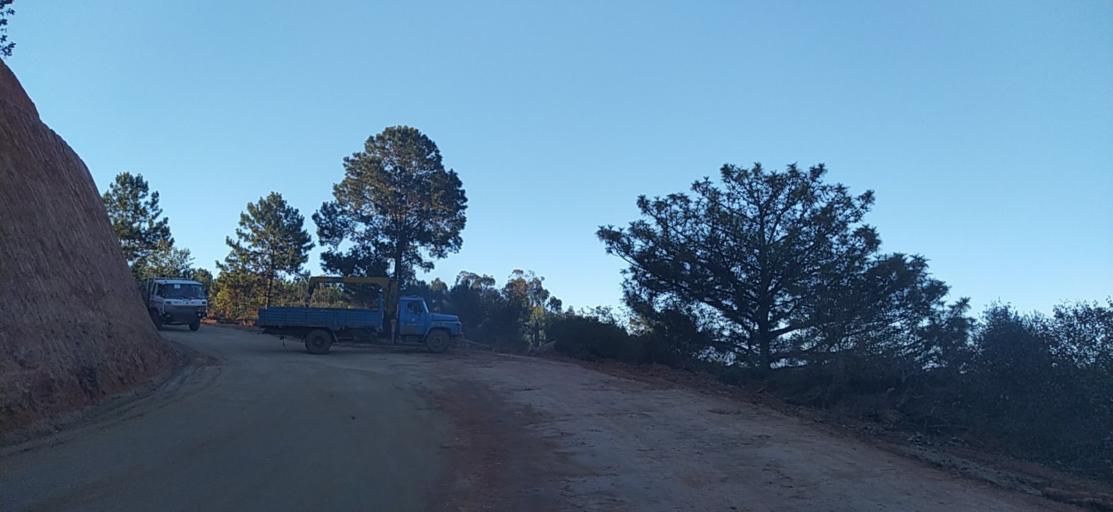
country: MG
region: Analamanga
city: Anjozorobe
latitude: -18.5130
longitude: 48.2631
